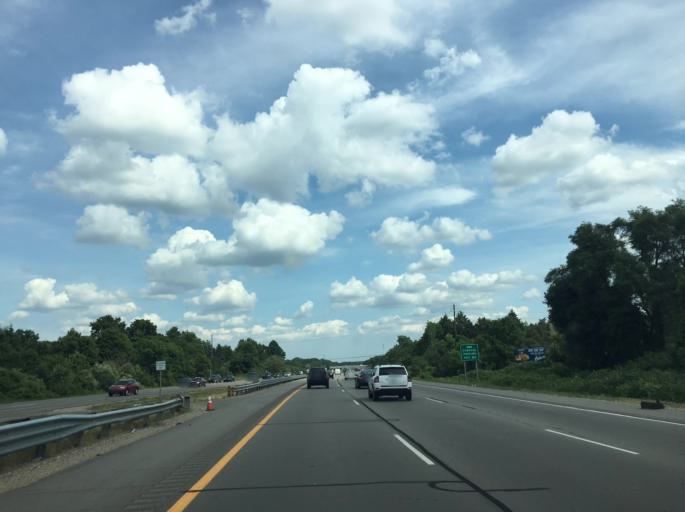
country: US
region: Michigan
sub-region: Oakland County
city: Clarkston
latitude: 42.7418
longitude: -83.3893
